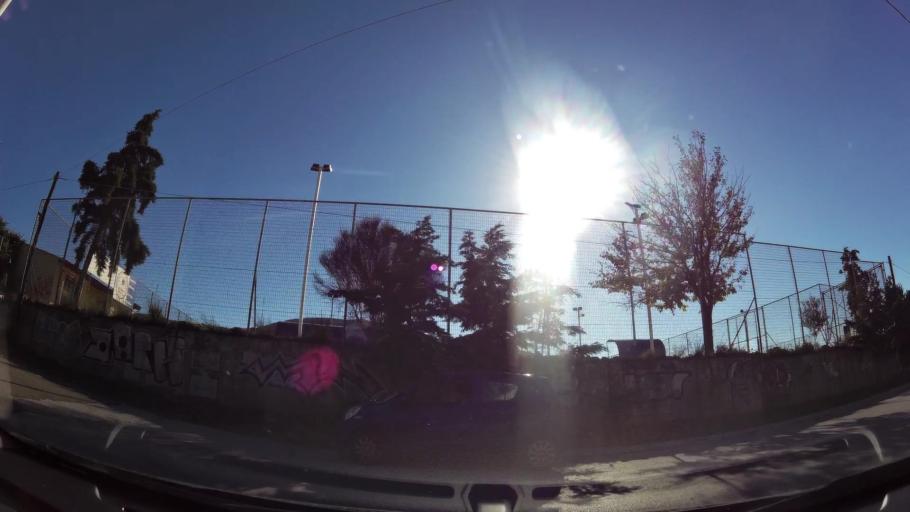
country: GR
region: Attica
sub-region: Nomarchia Anatolikis Attikis
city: Kalyvia Thorikou
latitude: 37.8348
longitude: 23.9348
